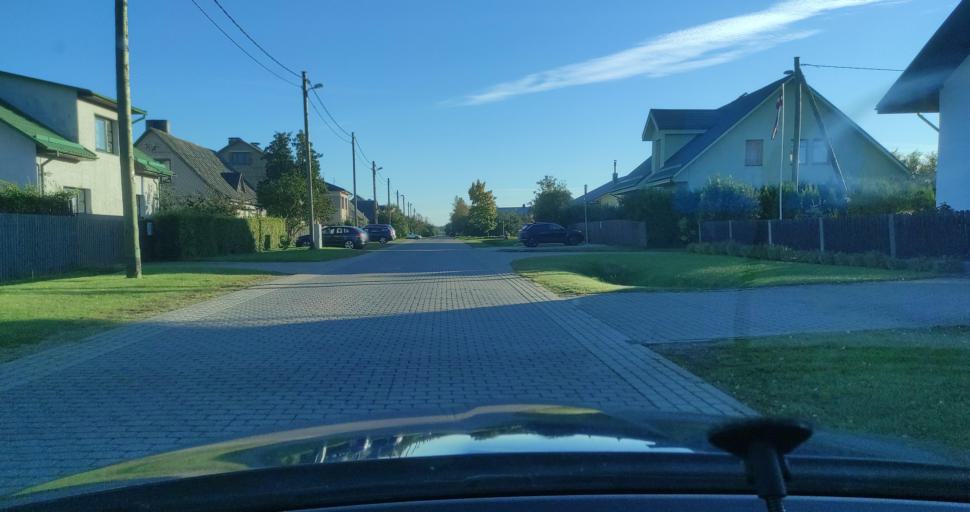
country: LV
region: Ventspils
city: Ventspils
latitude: 57.3735
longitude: 21.5773
